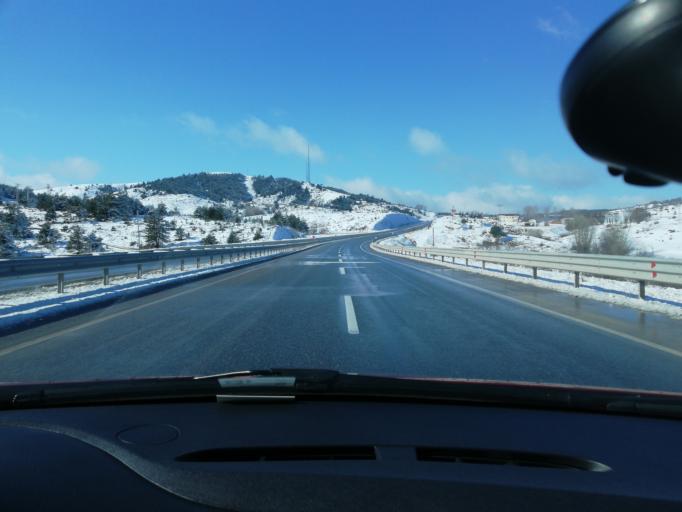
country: TR
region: Kastamonu
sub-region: Cide
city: Kastamonu
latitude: 41.3584
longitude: 33.6757
